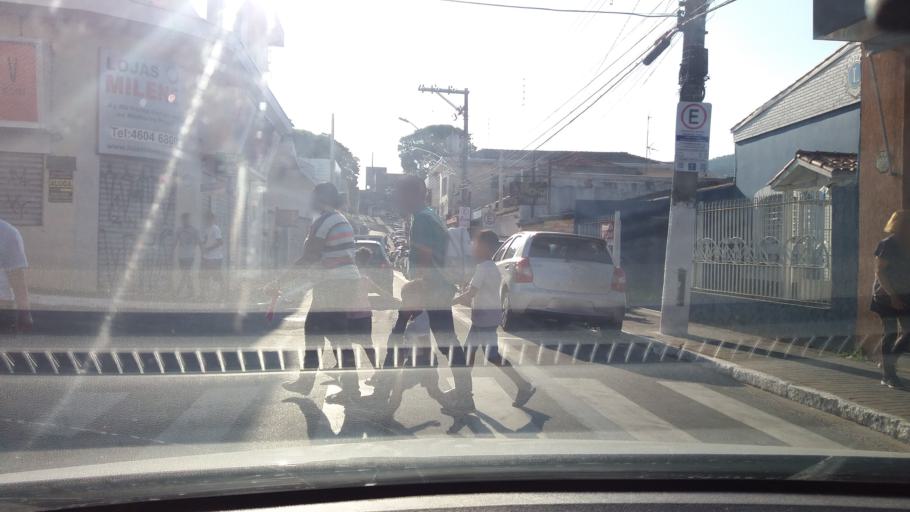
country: BR
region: Sao Paulo
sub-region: Mairipora
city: Mairipora
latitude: -23.3191
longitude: -46.5860
